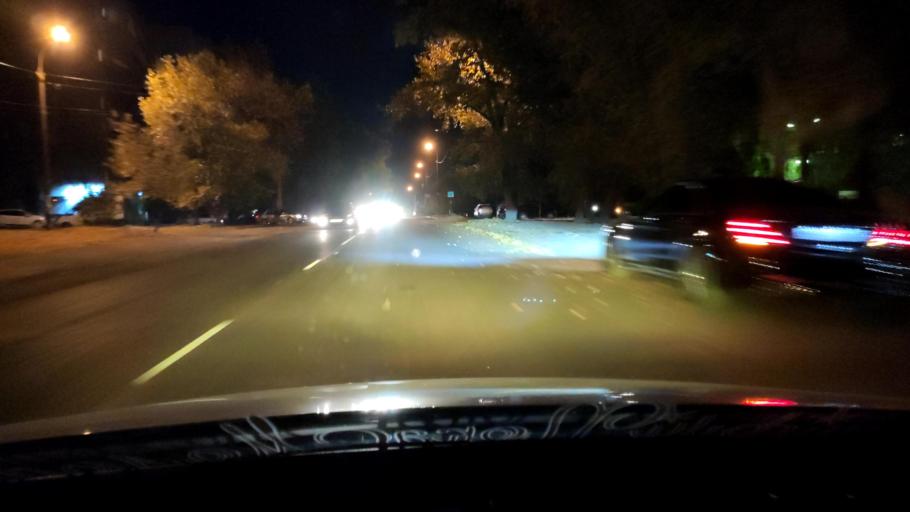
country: RU
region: Voronezj
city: Podgornoye
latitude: 51.6969
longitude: 39.1448
